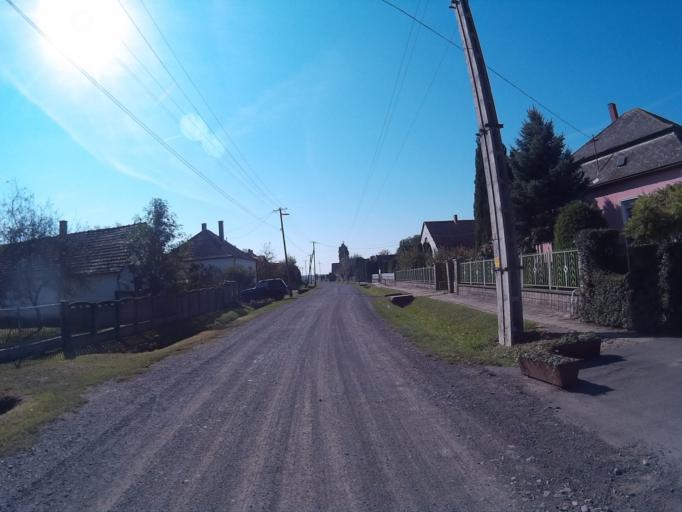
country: HU
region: Vas
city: Jak
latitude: 47.0858
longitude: 16.6280
